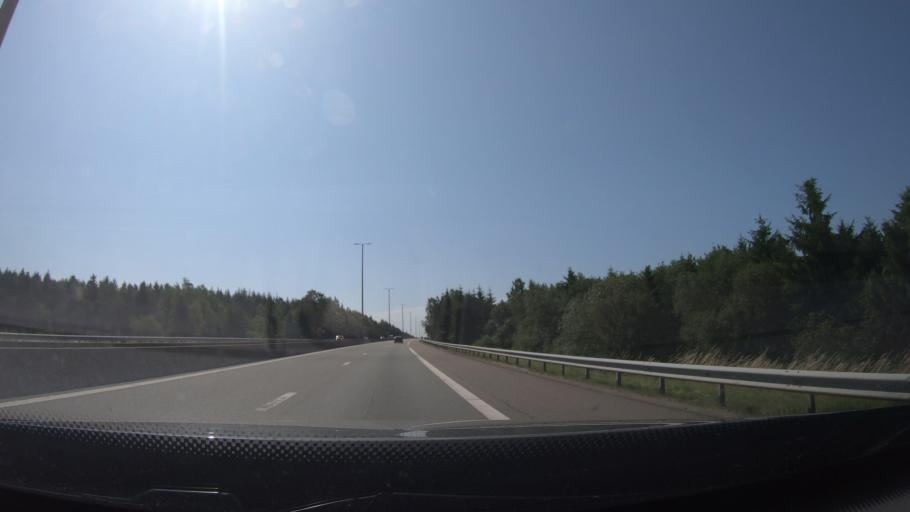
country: BE
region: Wallonia
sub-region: Province de Liege
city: Malmedy
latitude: 50.4675
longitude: 5.9897
